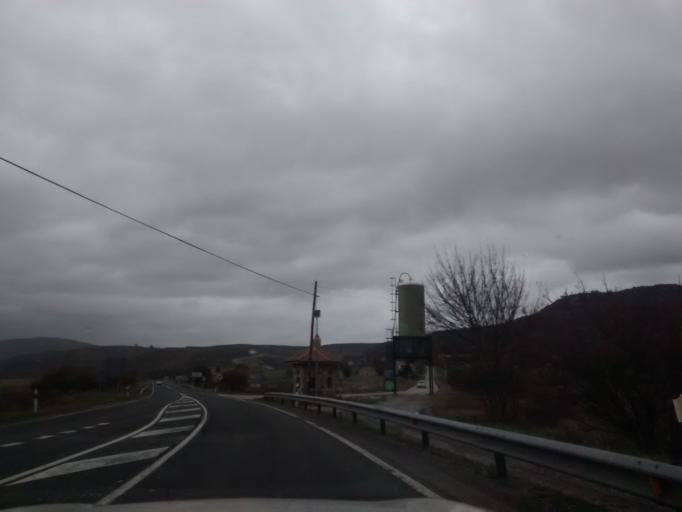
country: ES
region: Castille and Leon
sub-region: Provincia de Burgos
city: Arija
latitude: 43.0226
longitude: -3.8569
